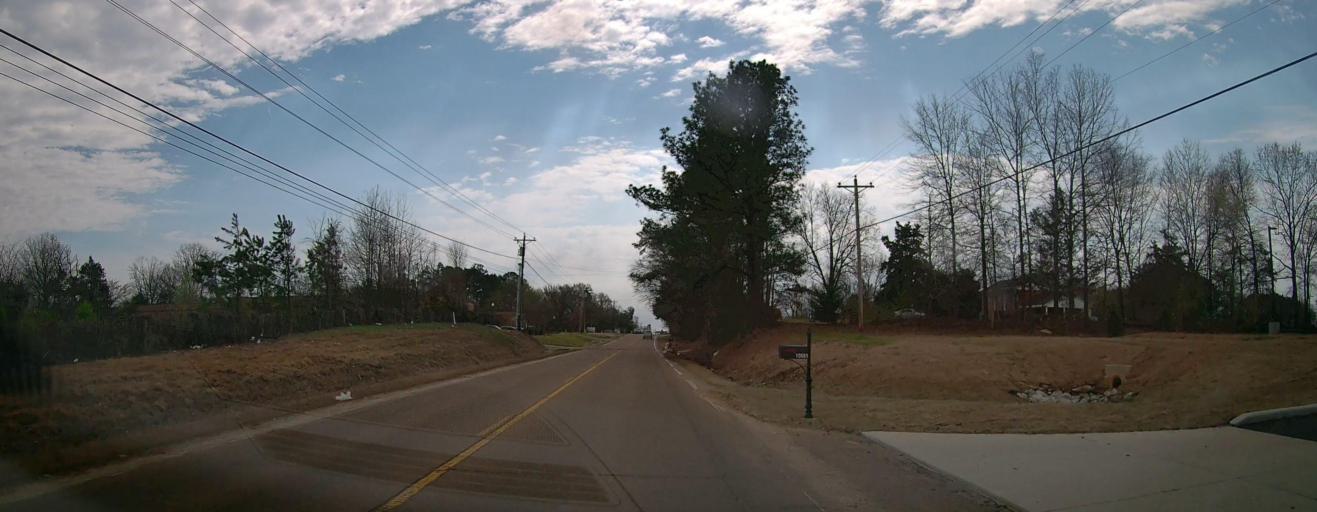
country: US
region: Mississippi
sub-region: De Soto County
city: Olive Branch
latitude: 34.9369
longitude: -89.8006
